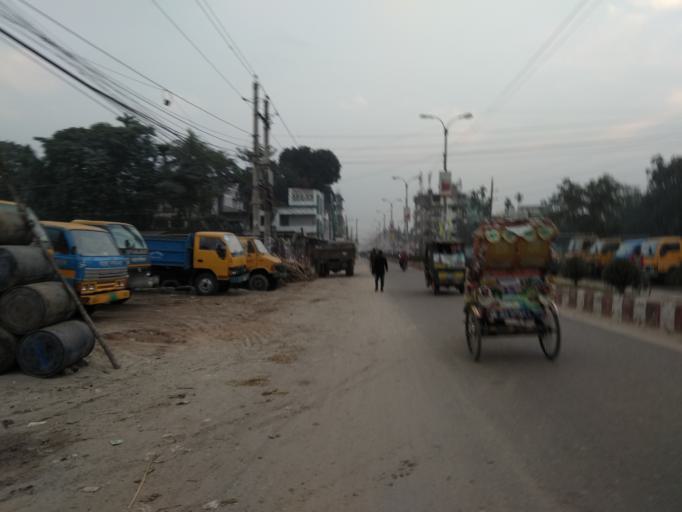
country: BD
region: Rangpur Division
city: Rangpur
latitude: 25.7340
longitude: 89.2548
